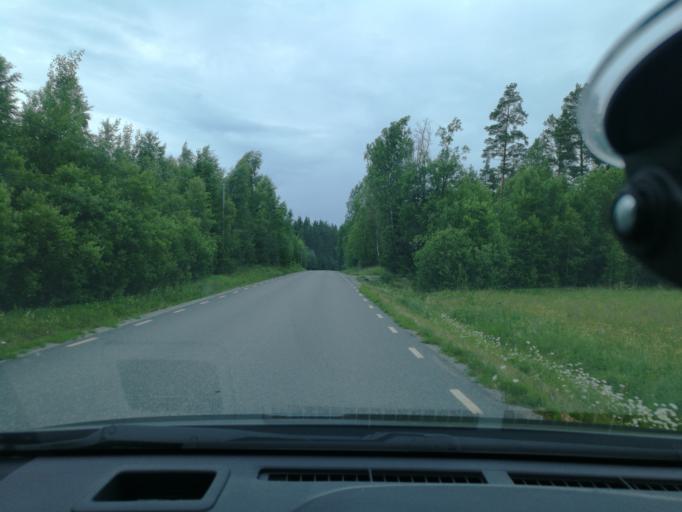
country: SE
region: Vaestmanland
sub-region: Vasteras
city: Skultuna
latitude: 59.8064
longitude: 16.3421
